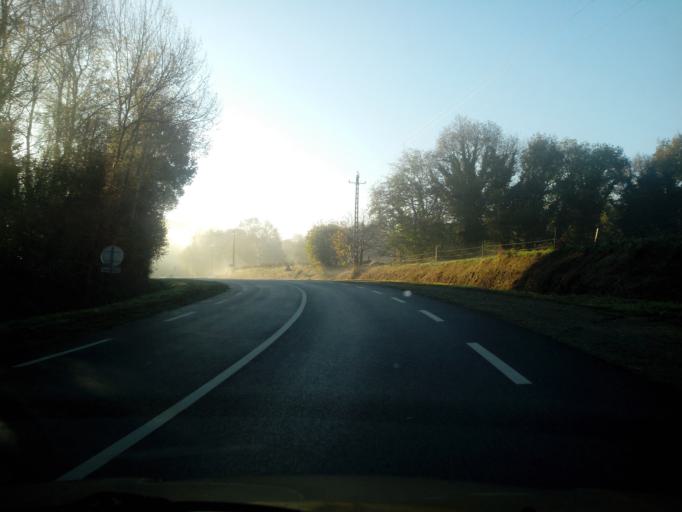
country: FR
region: Brittany
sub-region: Departement du Morbihan
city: Pluherlin
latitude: 47.7086
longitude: -2.3377
